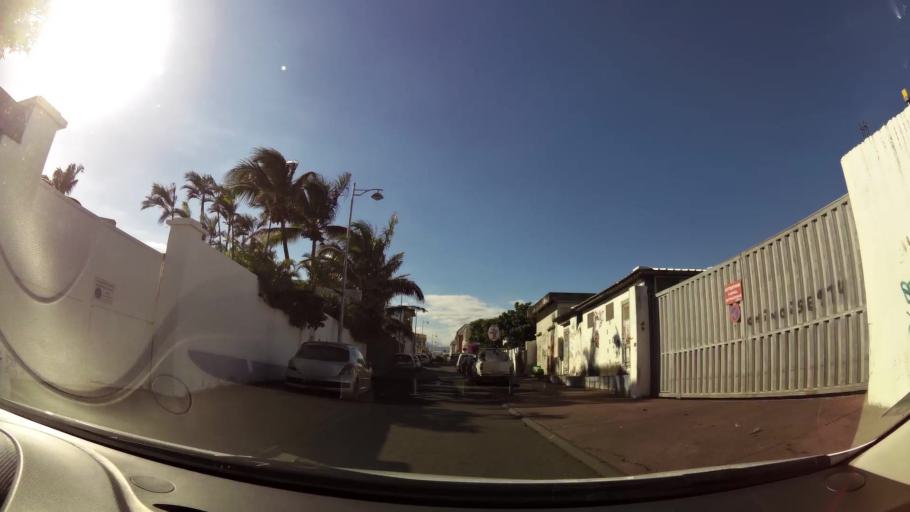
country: RE
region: Reunion
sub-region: Reunion
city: Saint-Pierre
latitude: -21.3419
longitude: 55.4699
